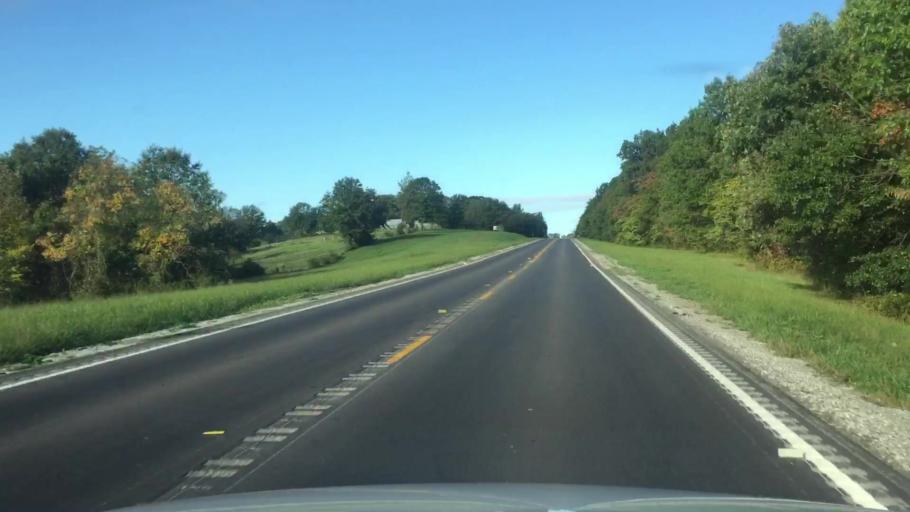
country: US
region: Missouri
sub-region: Howard County
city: New Franklin
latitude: 38.9974
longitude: -92.5863
